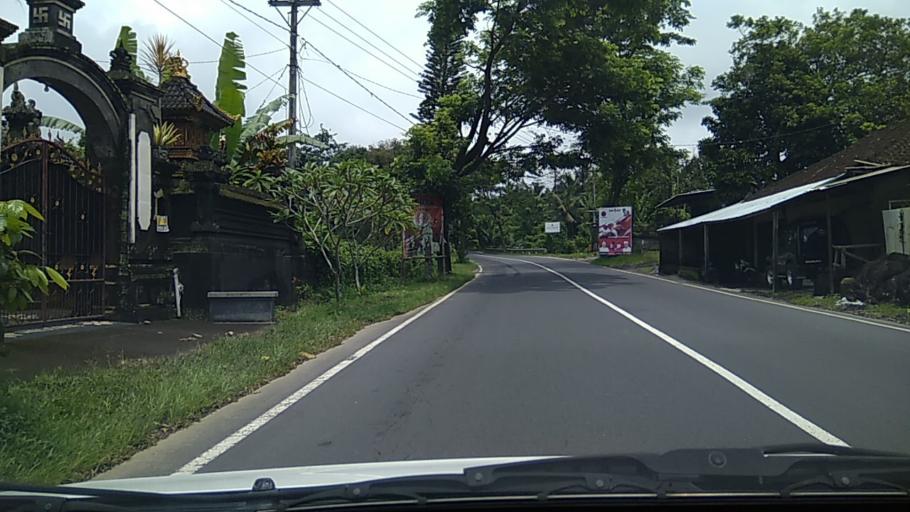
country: ID
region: Bali
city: Peneng
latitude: -8.3644
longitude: 115.1917
